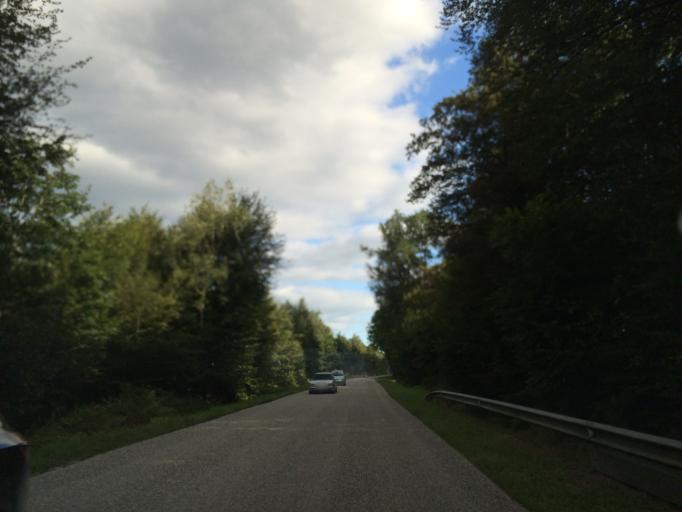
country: FR
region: Alsace
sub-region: Departement du Bas-Rhin
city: Betschdorf
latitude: 48.8768
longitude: 7.9282
